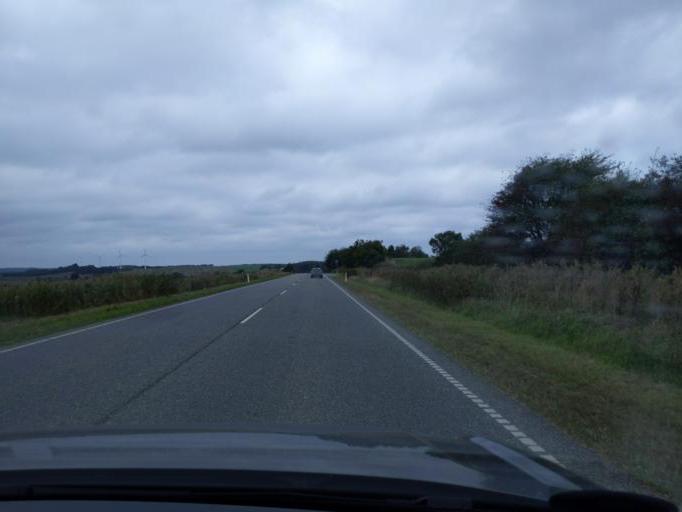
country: DK
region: North Denmark
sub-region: Mariagerfjord Kommune
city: Hobro
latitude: 56.5648
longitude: 9.8343
